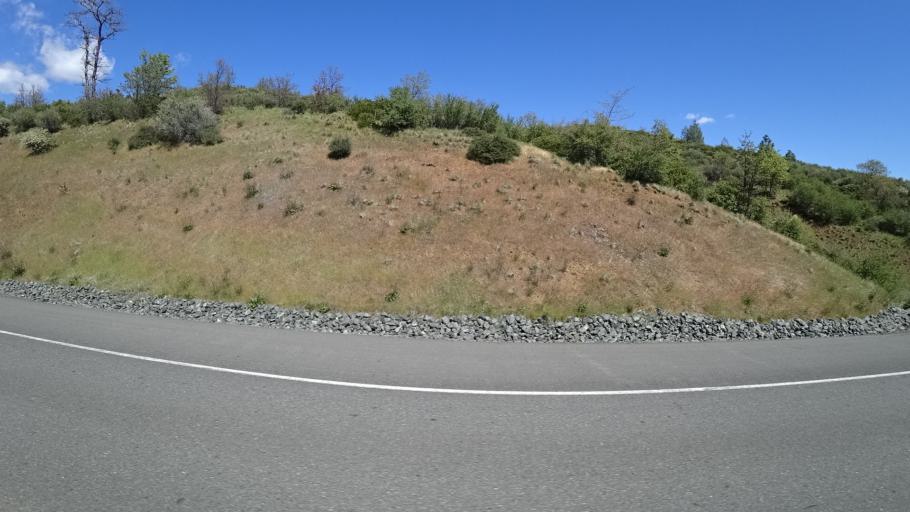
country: US
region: California
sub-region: Trinity County
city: Weaverville
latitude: 40.7391
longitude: -122.9667
